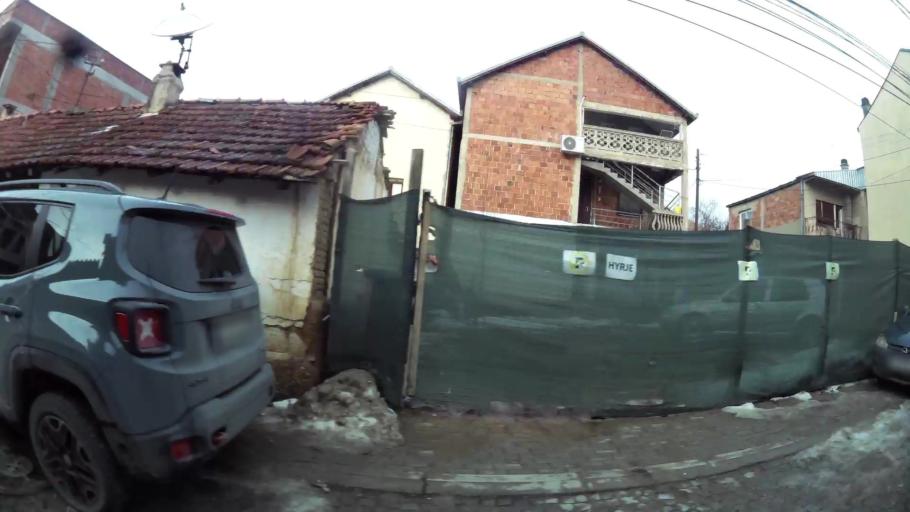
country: XK
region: Pristina
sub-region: Komuna e Prishtines
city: Pristina
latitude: 42.6693
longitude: 21.1689
